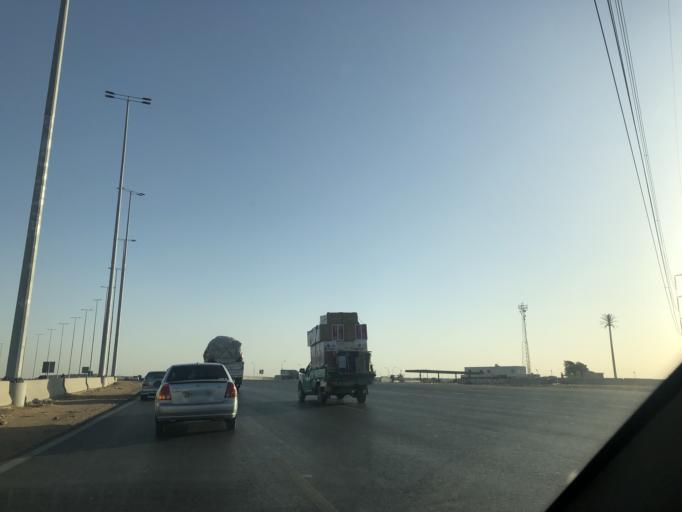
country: EG
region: Al Jizah
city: Al Jizah
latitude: 29.9421
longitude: 31.0989
